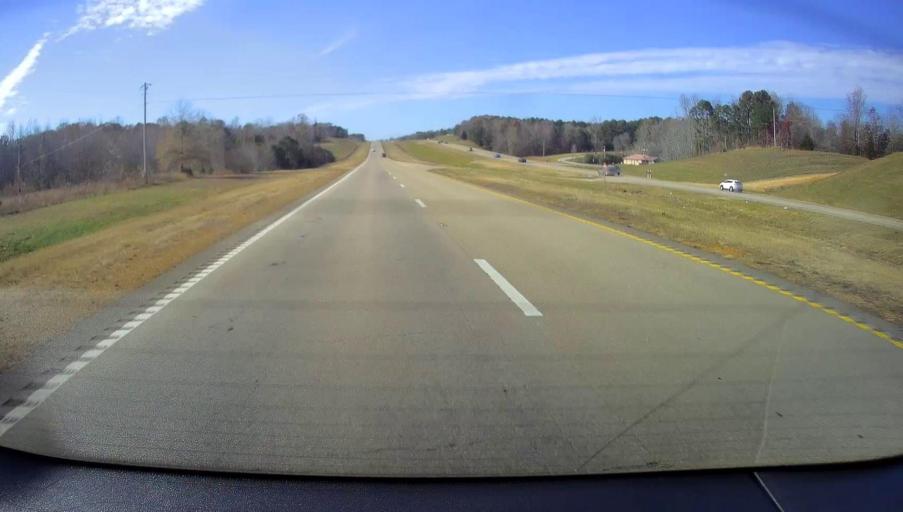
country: US
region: Mississippi
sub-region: Tippah County
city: Ripley
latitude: 34.9551
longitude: -88.9684
